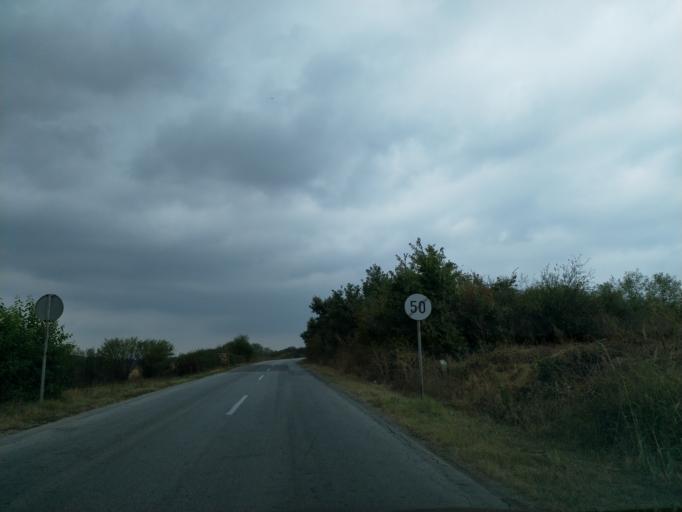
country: RS
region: Central Serbia
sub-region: Pomoravski Okrug
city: Jagodina
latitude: 44.0104
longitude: 21.2015
